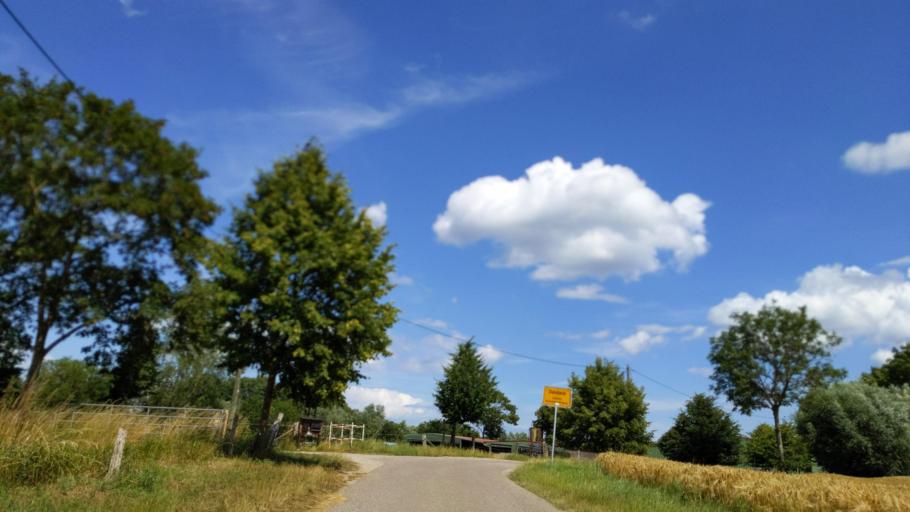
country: DE
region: Mecklenburg-Vorpommern
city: Klutz
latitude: 53.9962
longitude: 11.1353
